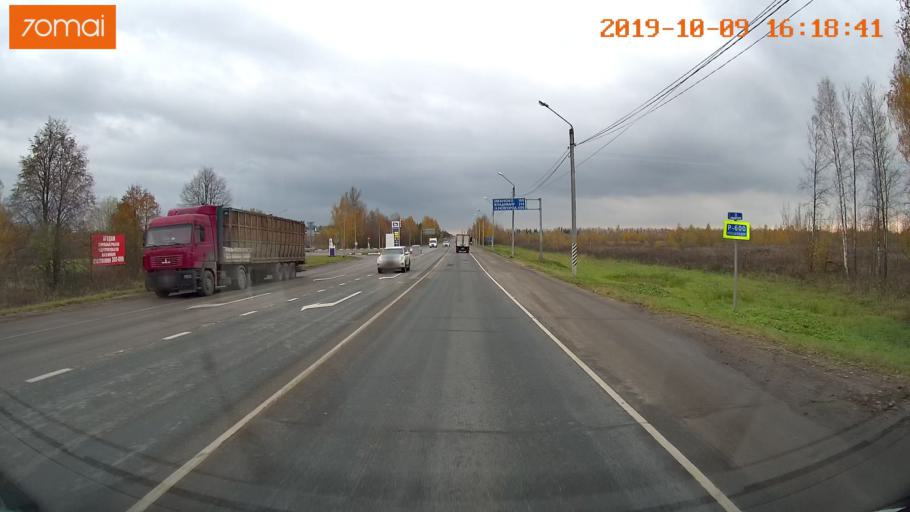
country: RU
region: Kostroma
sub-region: Kostromskoy Rayon
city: Kostroma
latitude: 57.7262
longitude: 40.8962
